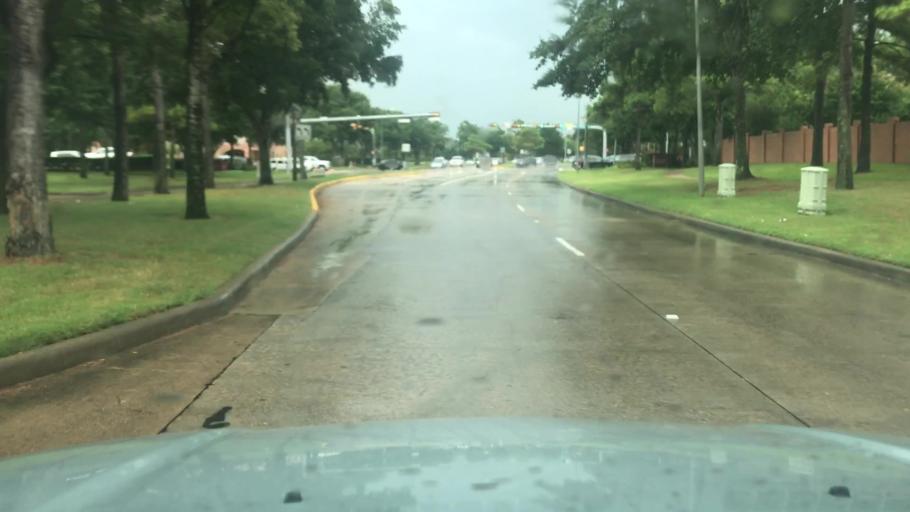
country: US
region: Texas
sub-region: Fort Bend County
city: Cinco Ranch
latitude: 29.7389
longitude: -95.7829
